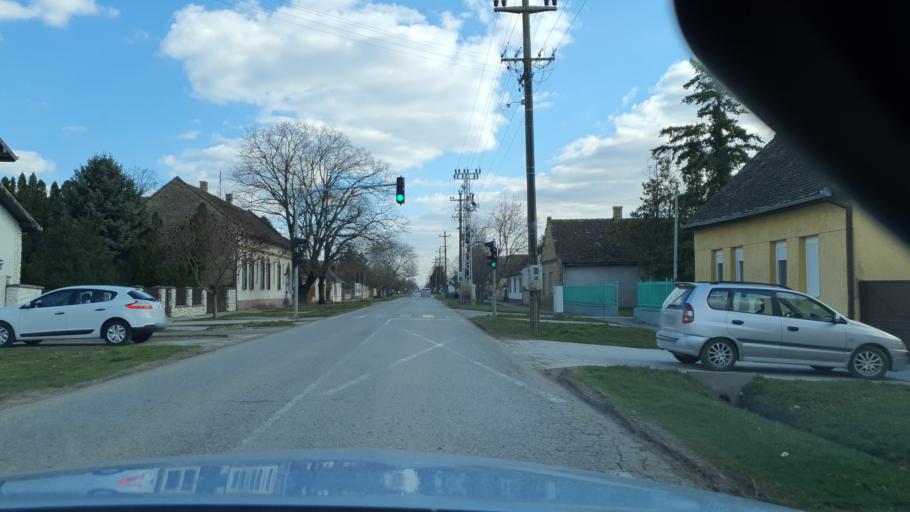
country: RS
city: Ravno Selo
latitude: 45.4497
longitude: 19.6199
